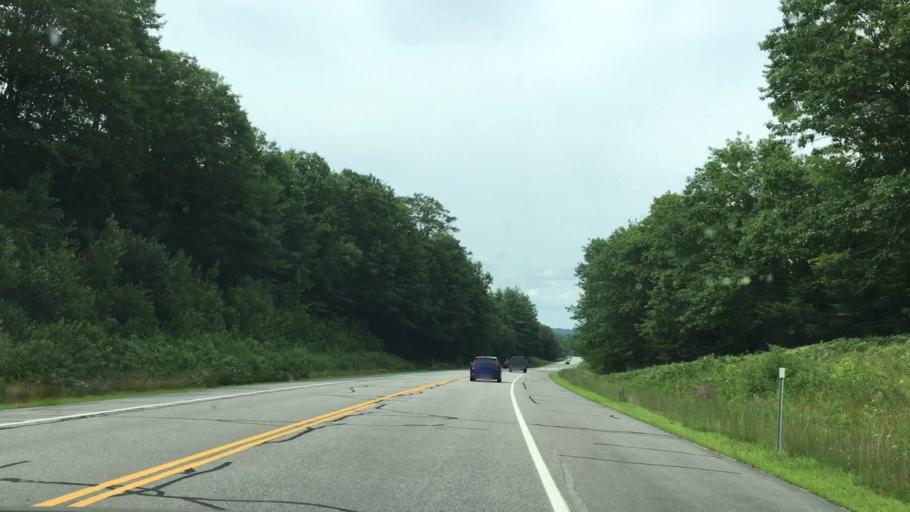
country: US
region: New Hampshire
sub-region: Hillsborough County
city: Hillsborough
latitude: 43.0732
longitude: -71.9169
